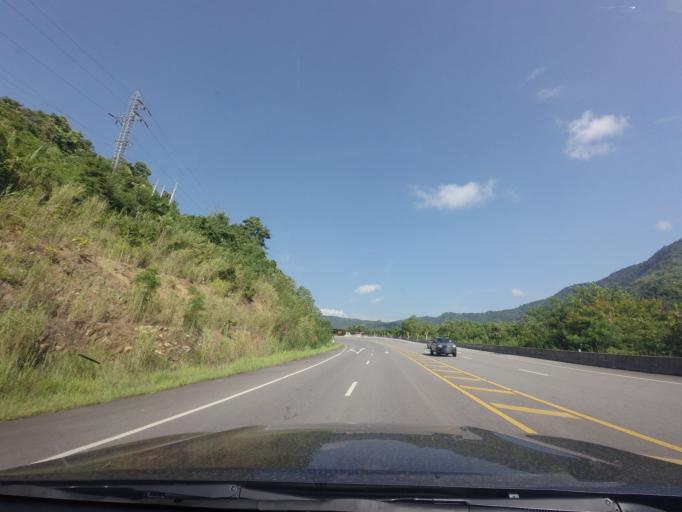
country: TH
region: Phetchabun
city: Lom Sak
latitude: 16.7721
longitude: 101.1260
